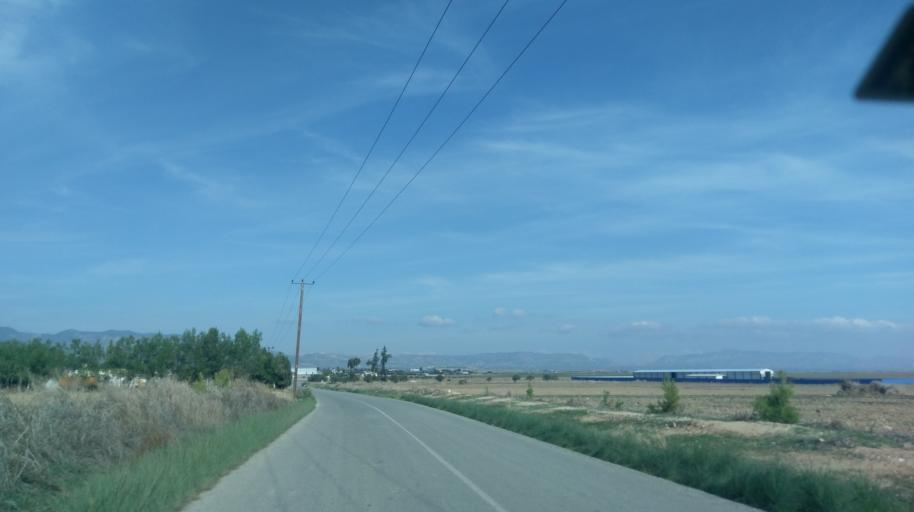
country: CY
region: Ammochostos
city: Lefkonoiko
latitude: 35.2076
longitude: 33.6193
